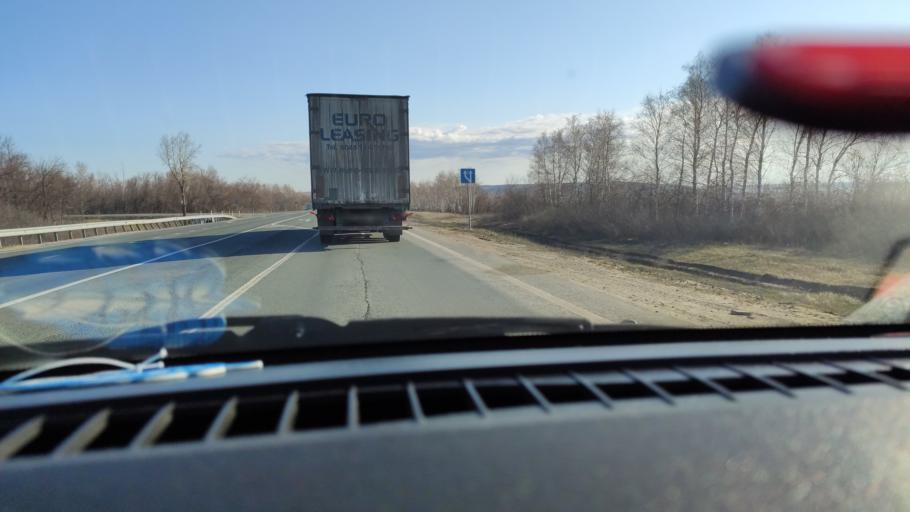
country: RU
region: Saratov
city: Dukhovnitskoye
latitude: 52.6810
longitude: 48.2328
